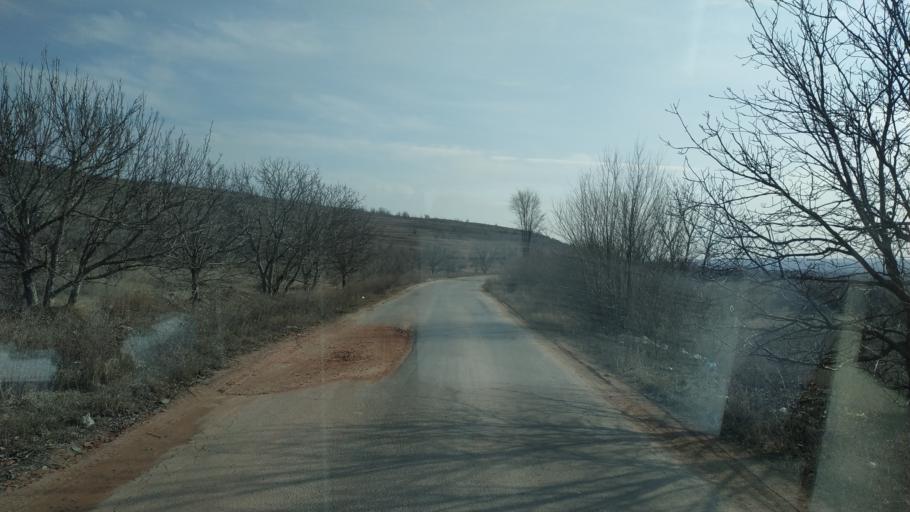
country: MD
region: Chisinau
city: Singera
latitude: 46.9231
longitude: 29.0913
